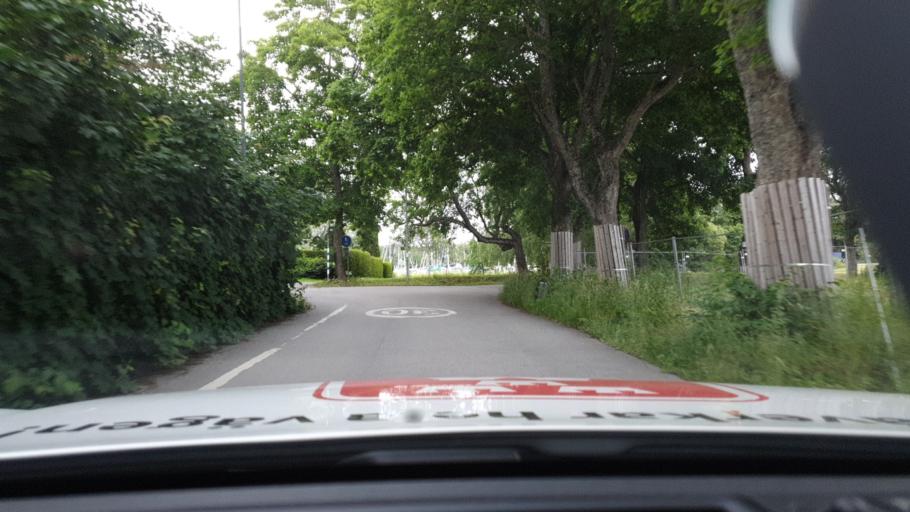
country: SE
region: Stockholm
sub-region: Osterakers Kommun
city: Akersberga
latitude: 59.4634
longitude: 18.3168
